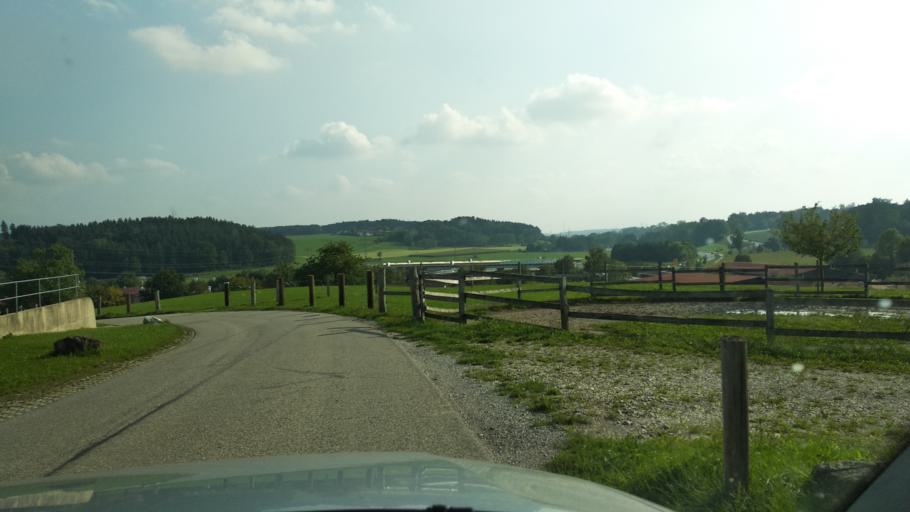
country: DE
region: Bavaria
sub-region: Upper Bavaria
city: Ebersberg
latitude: 48.0830
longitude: 11.9863
